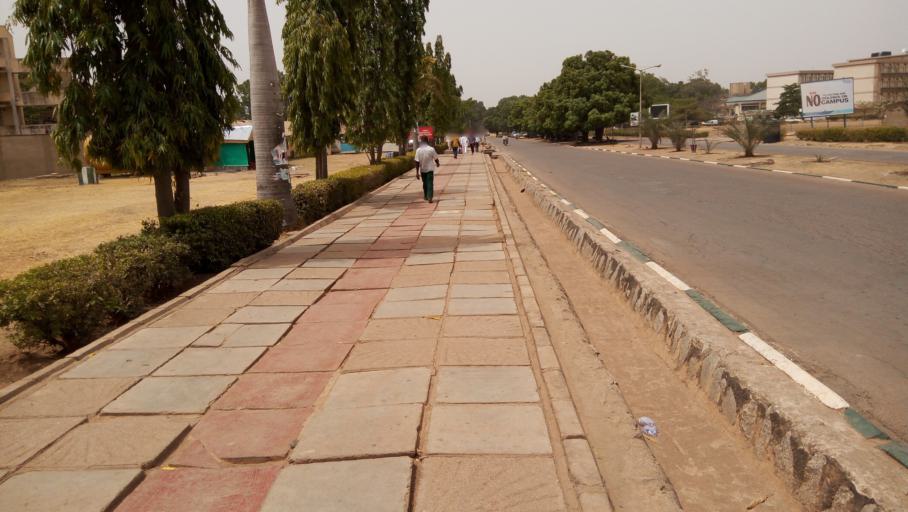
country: NG
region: Kaduna
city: Zaria
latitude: 11.1563
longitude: 7.6523
